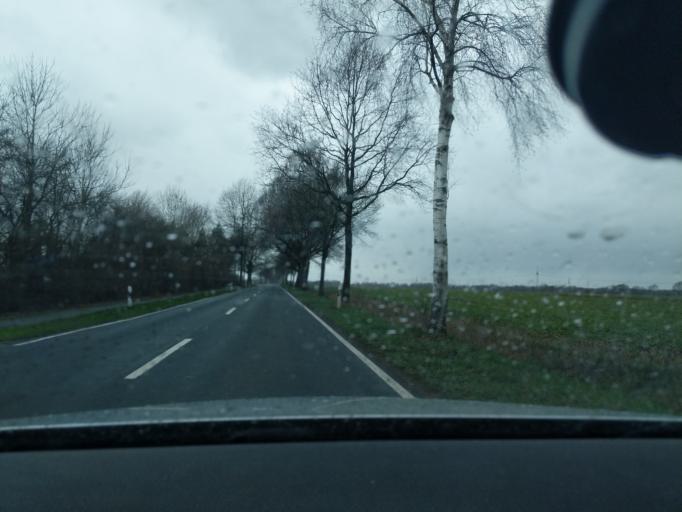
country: DE
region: Lower Saxony
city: Bargstedt
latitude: 53.4616
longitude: 9.4414
